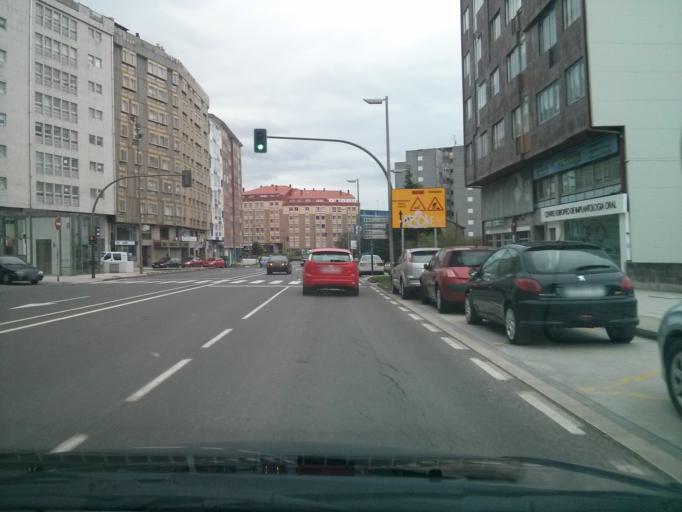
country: ES
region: Galicia
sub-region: Provincia da Coruna
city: Santiago de Compostela
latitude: 42.8707
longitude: -8.5500
